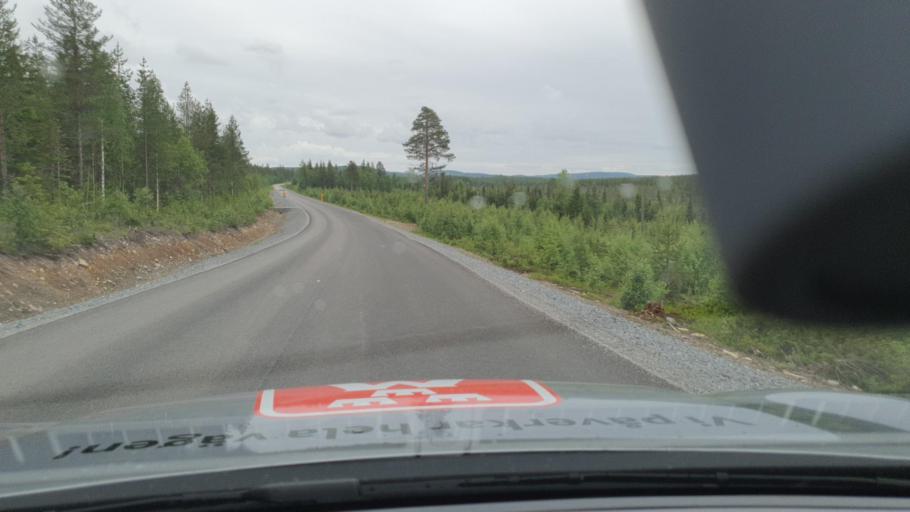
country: SE
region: Norrbotten
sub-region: Overtornea Kommun
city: OEvertornea
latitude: 66.5903
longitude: 23.3175
